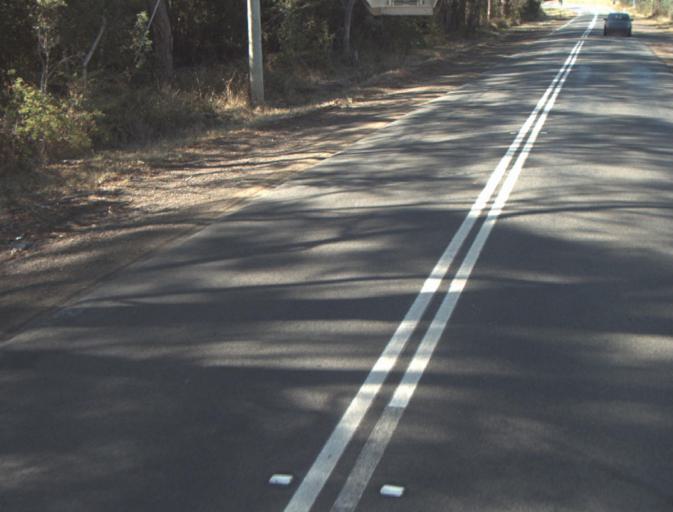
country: AU
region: Tasmania
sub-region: Launceston
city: Mayfield
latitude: -41.3664
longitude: 147.1426
